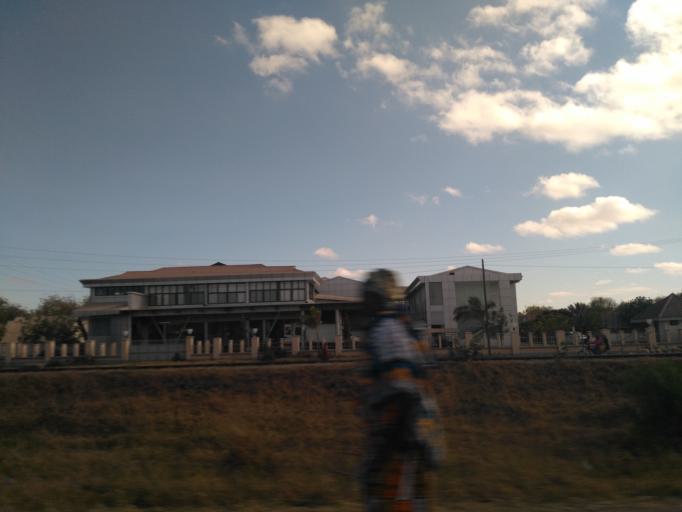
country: TZ
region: Dodoma
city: Dodoma
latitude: -6.1829
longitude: 35.7418
